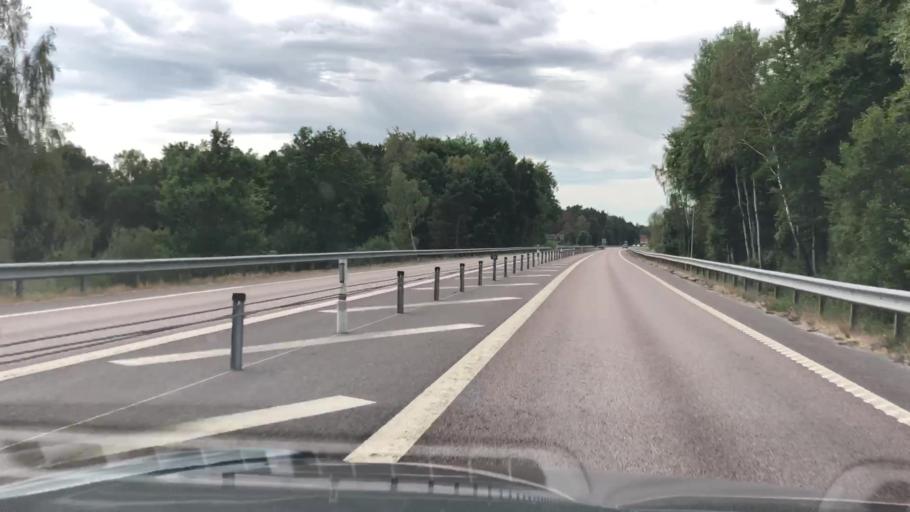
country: SE
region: Kalmar
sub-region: Torsas Kommun
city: Torsas
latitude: 56.3045
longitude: 16.0088
